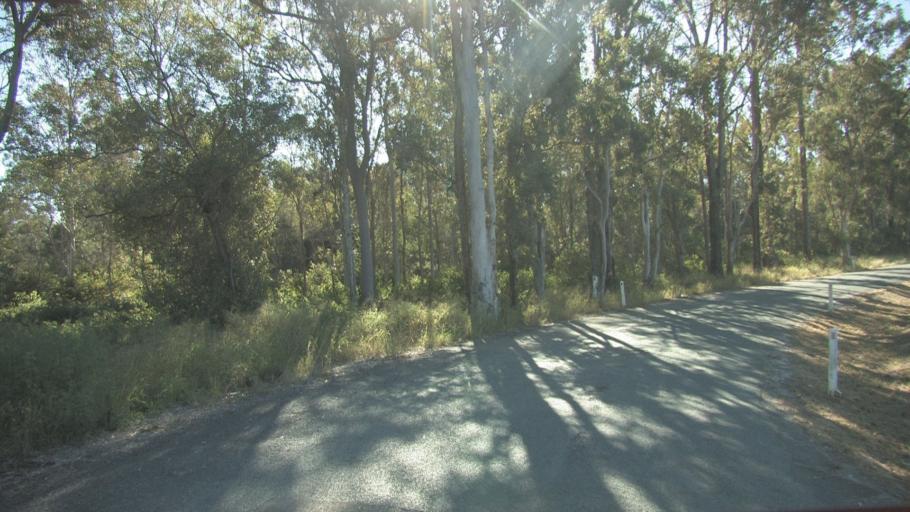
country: AU
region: Queensland
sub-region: Logan
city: Logan Reserve
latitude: -27.7545
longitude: 153.1378
